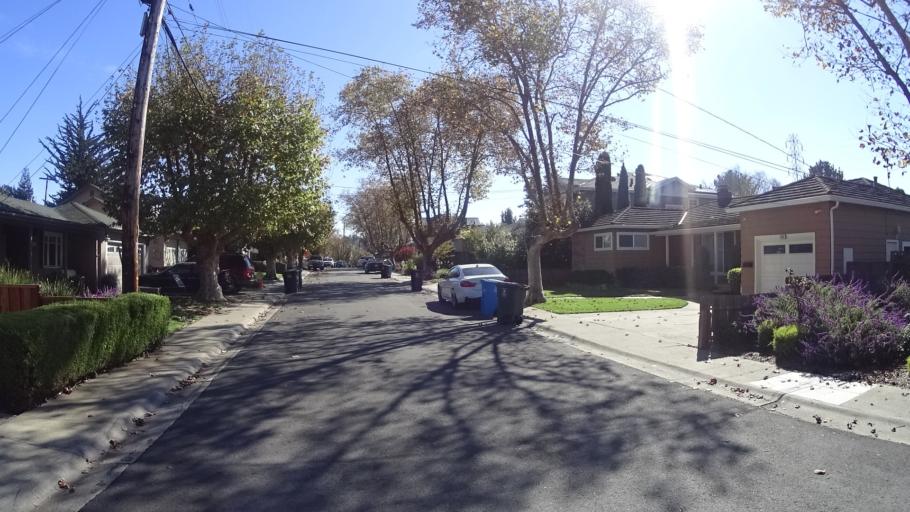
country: US
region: California
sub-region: San Mateo County
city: Hillsborough
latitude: 37.5736
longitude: -122.3974
